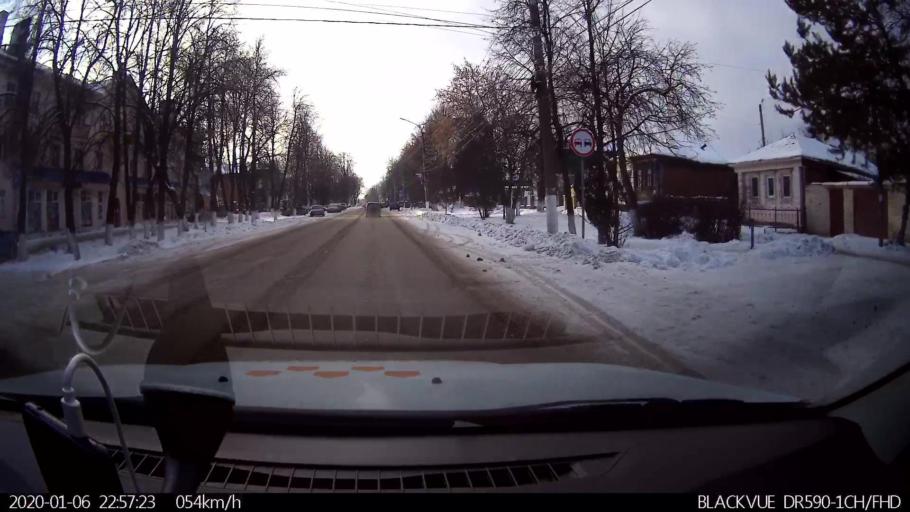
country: RU
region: Nizjnij Novgorod
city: Bogorodsk
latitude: 56.1078
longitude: 43.5253
